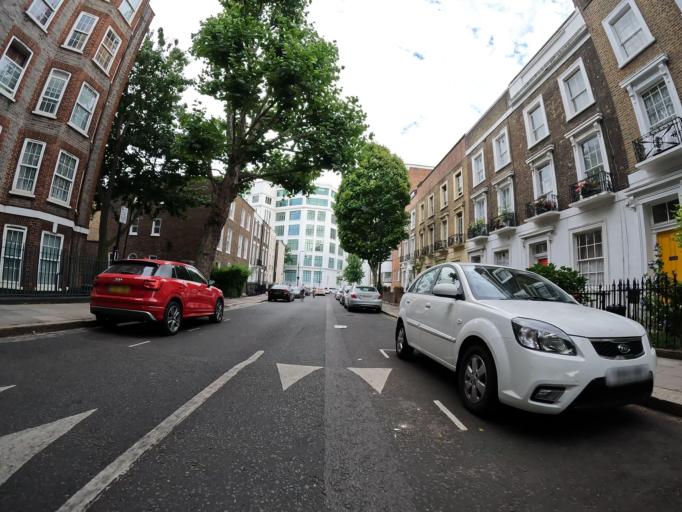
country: GB
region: England
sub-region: Greater London
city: Camden Town
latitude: 51.5348
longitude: -0.1406
